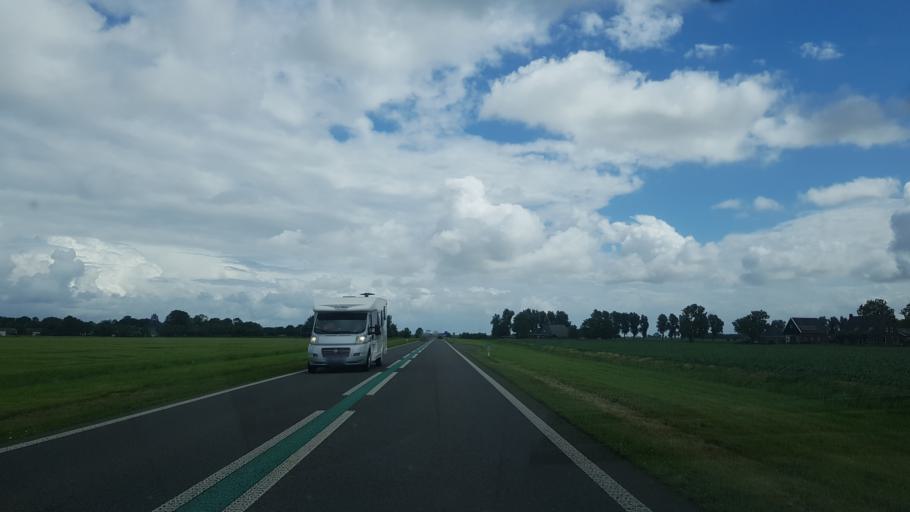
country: NL
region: Friesland
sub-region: Gemeente Dongeradeel
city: Anjum
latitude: 53.3659
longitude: 6.0857
